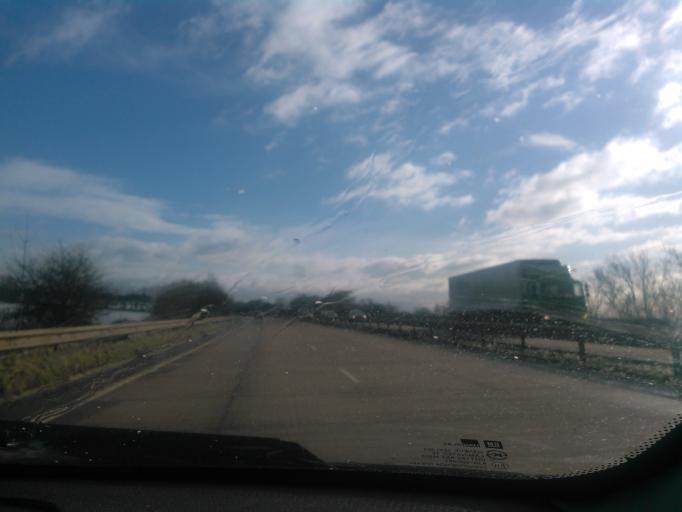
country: GB
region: England
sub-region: Staffordshire
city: Cheadle
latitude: 52.9461
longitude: -2.0089
